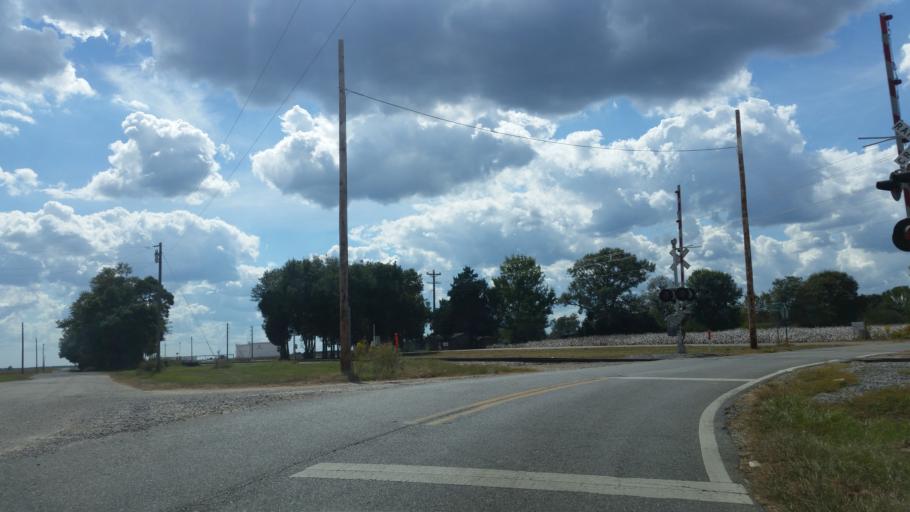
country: US
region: Alabama
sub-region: Escambia County
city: Atmore
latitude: 30.8860
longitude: -87.5056
